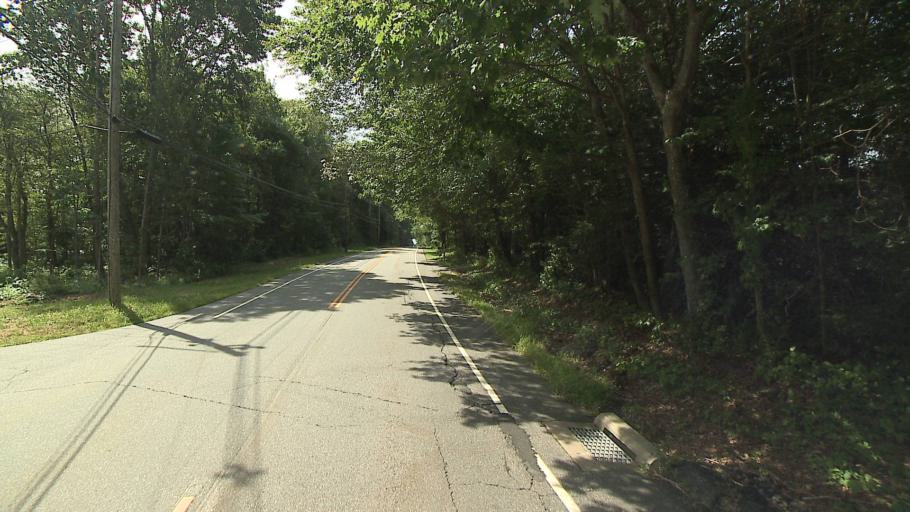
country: US
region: Connecticut
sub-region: Litchfield County
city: Bethlehem Village
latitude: 41.6599
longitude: -73.1984
